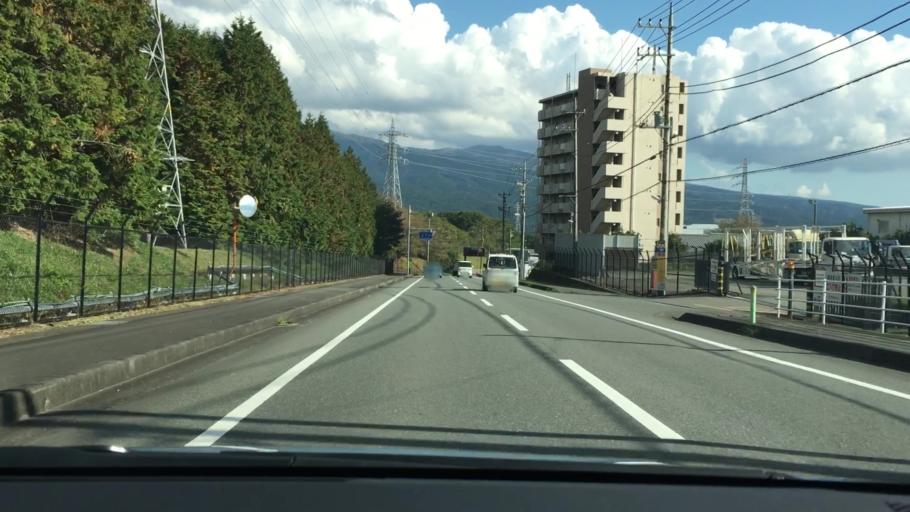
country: JP
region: Shizuoka
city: Gotemba
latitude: 35.2210
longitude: 138.9045
